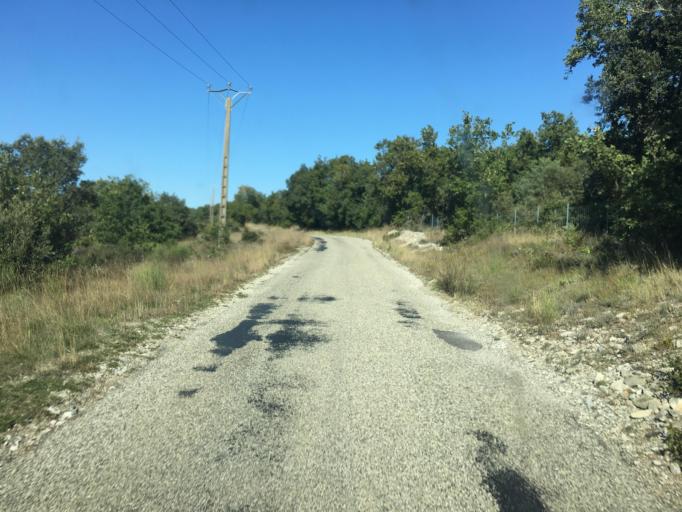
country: FR
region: Languedoc-Roussillon
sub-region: Departement du Gard
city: Montaren-et-Saint-Mediers
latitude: 44.1323
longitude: 4.3118
